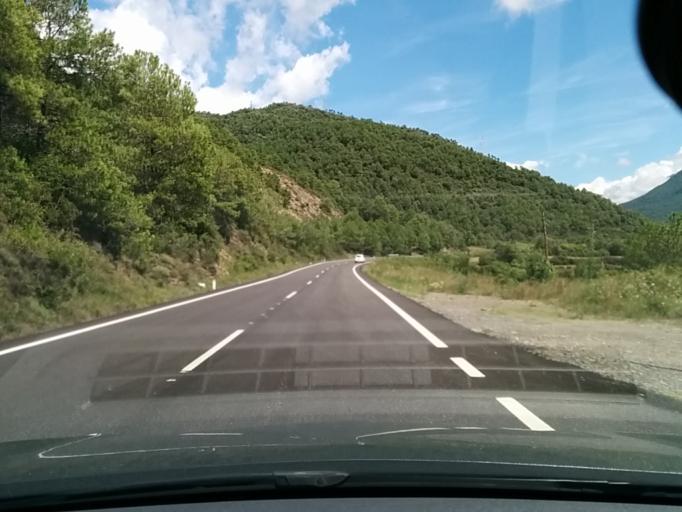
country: ES
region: Aragon
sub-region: Provincia de Huesca
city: Labuerda
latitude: 42.4622
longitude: 0.1359
